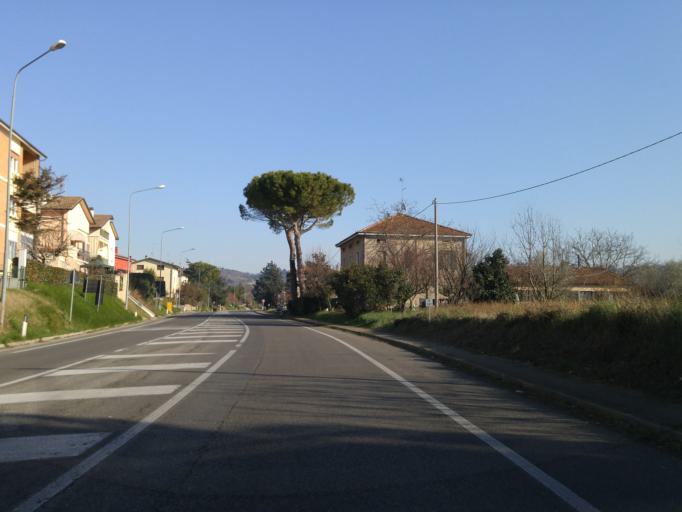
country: IT
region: The Marches
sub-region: Provincia di Pesaro e Urbino
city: Gradara
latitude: 43.9477
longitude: 12.7956
